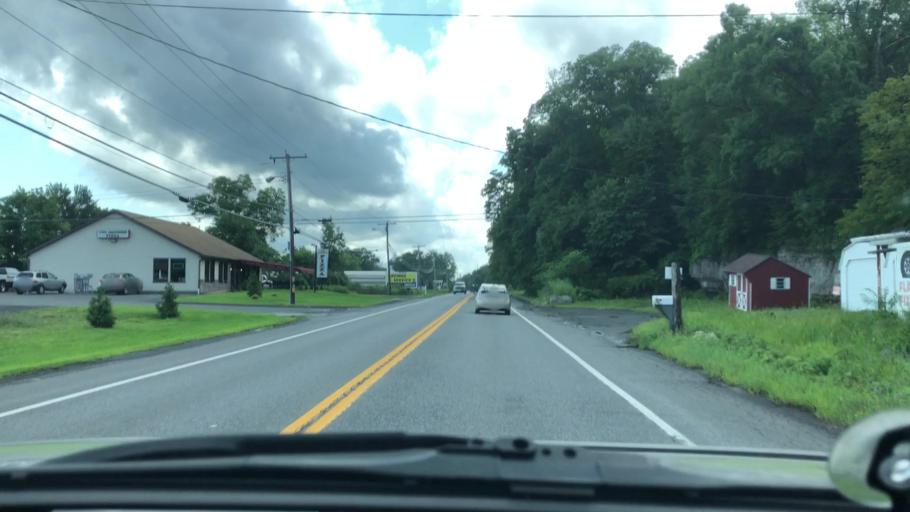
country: US
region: New York
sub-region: Ulster County
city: Saugerties
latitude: 42.1002
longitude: -73.9704
